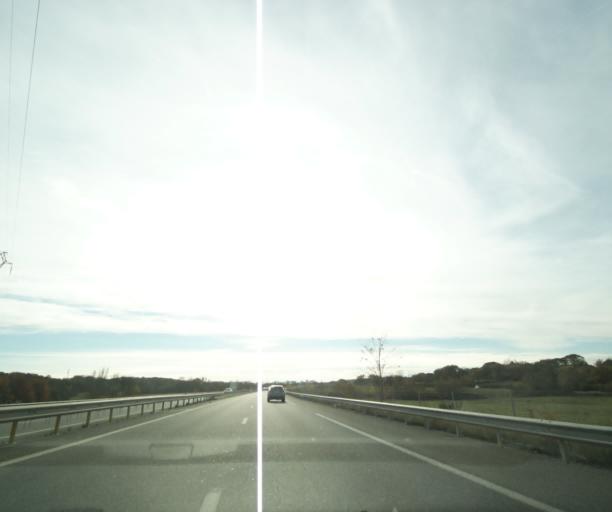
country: FR
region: Midi-Pyrenees
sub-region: Departement de la Haute-Garonne
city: La Salvetat-Saint-Gilles
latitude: 43.5933
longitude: 1.2763
